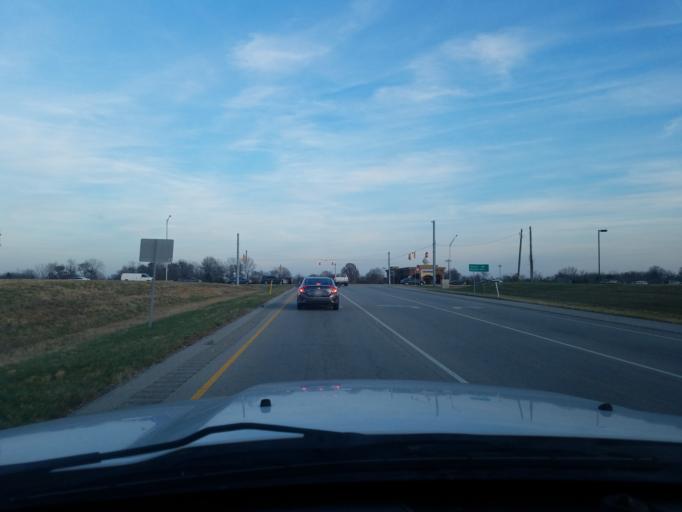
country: US
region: Indiana
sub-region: Clark County
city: Clarksville
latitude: 38.3427
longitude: -85.8004
